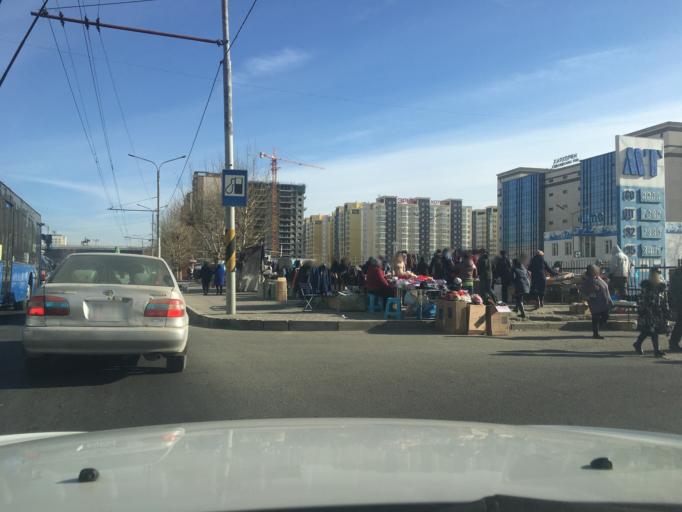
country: MN
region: Ulaanbaatar
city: Ulaanbaatar
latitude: 47.9112
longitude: 106.8346
